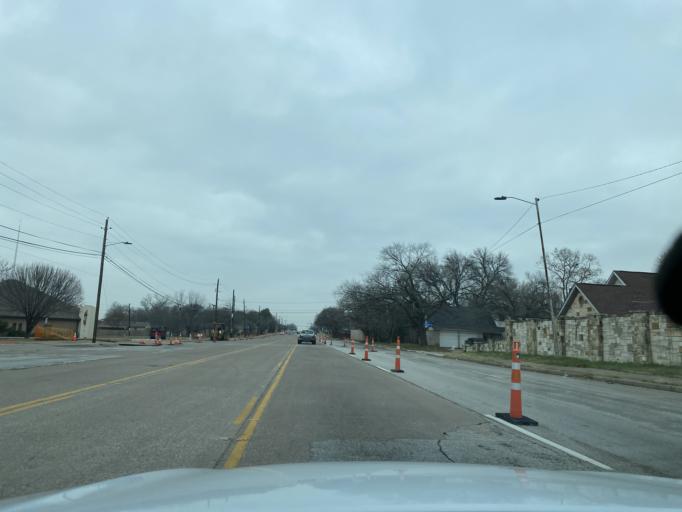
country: US
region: Texas
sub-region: Tarrant County
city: Arlington
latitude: 32.7099
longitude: -97.0975
